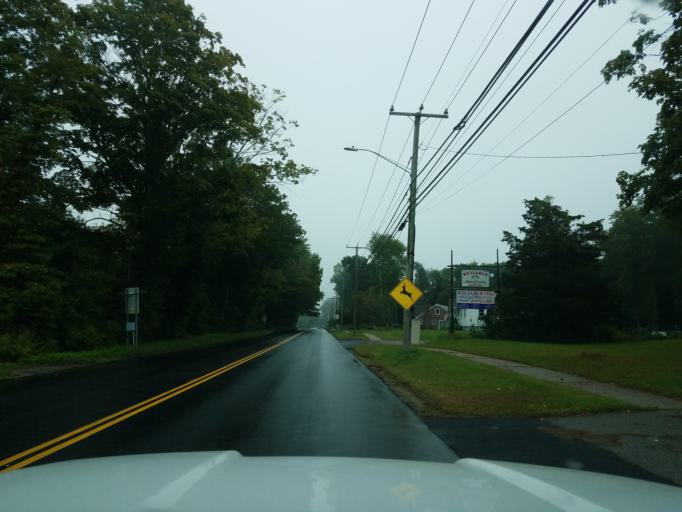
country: US
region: Connecticut
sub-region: New London County
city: Colchester
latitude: 41.5746
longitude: -72.3142
